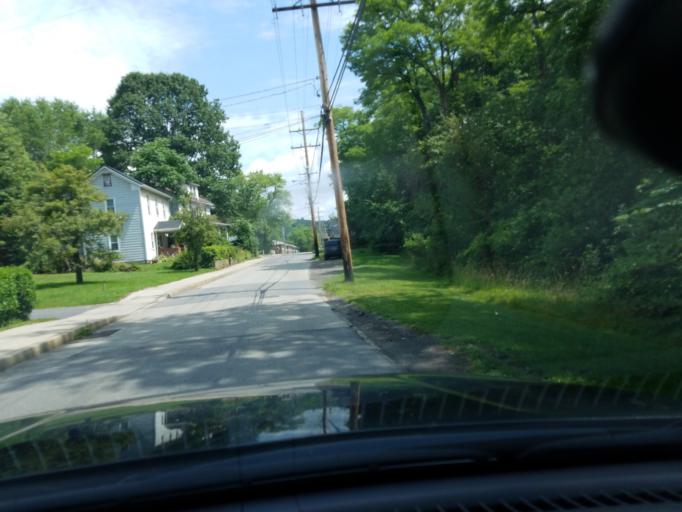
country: US
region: Pennsylvania
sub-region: Cambria County
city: Johnstown
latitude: 40.3539
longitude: -78.9424
